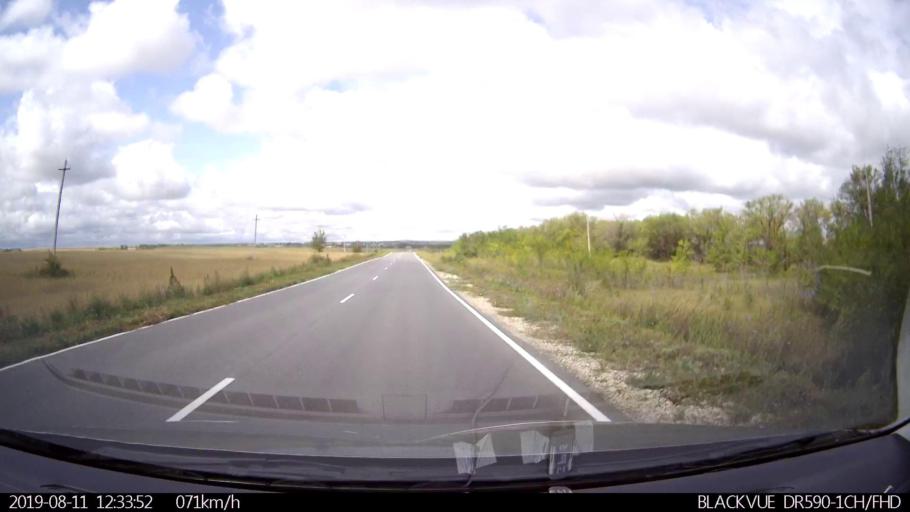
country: RU
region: Ulyanovsk
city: Ignatovka
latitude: 53.8127
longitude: 47.8503
